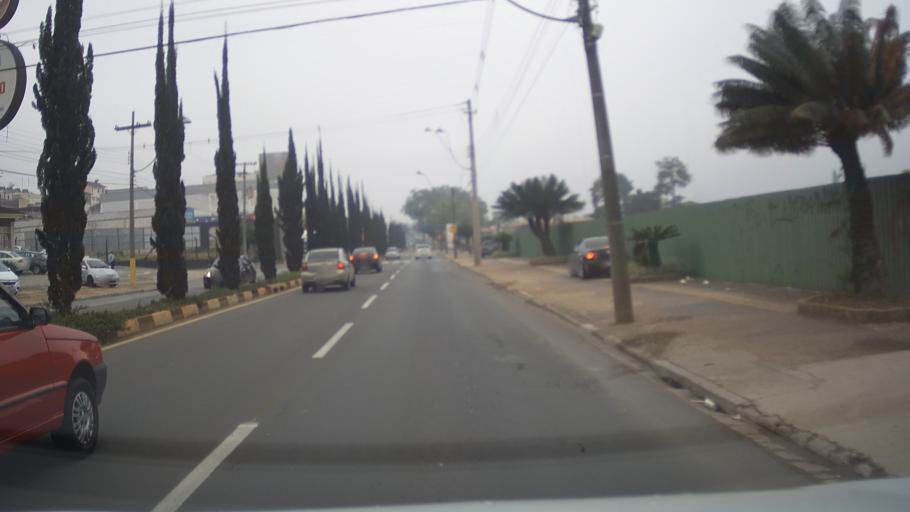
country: BR
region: Sao Paulo
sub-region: Itatiba
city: Itatiba
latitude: -23.0212
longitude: -46.8423
